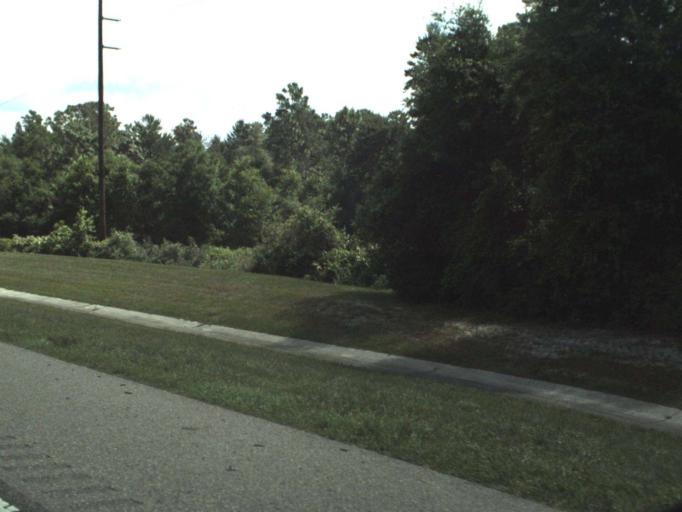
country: US
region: Florida
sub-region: Volusia County
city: Orange City
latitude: 28.9396
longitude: -81.2625
